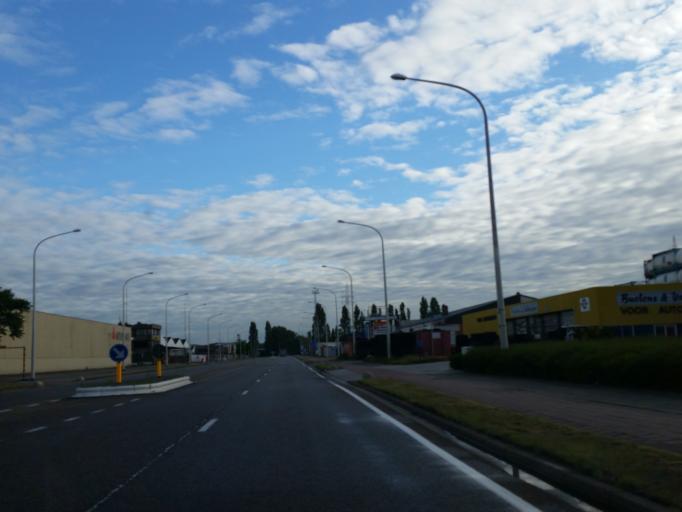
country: BE
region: Flanders
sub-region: Provincie Antwerpen
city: Antwerpen
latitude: 51.2685
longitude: 4.4007
